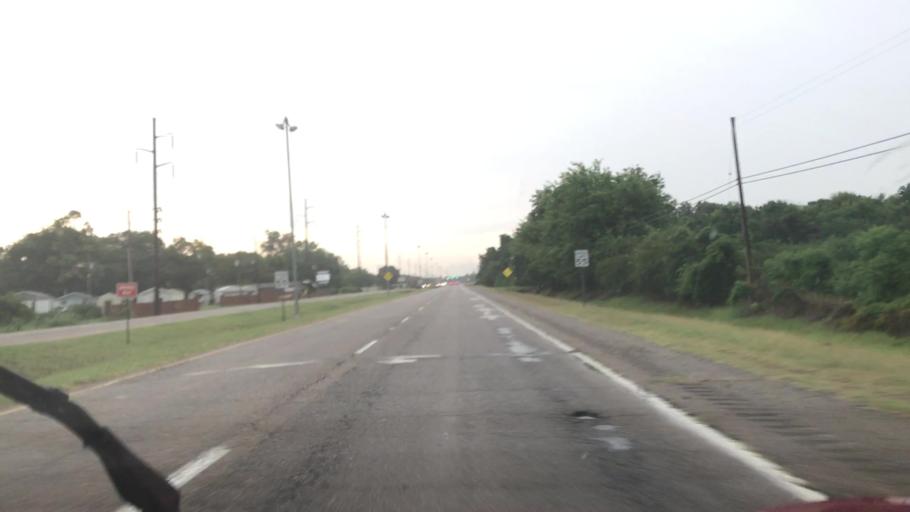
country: US
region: Louisiana
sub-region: Bossier Parish
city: Red Chute
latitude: 32.5389
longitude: -93.6551
